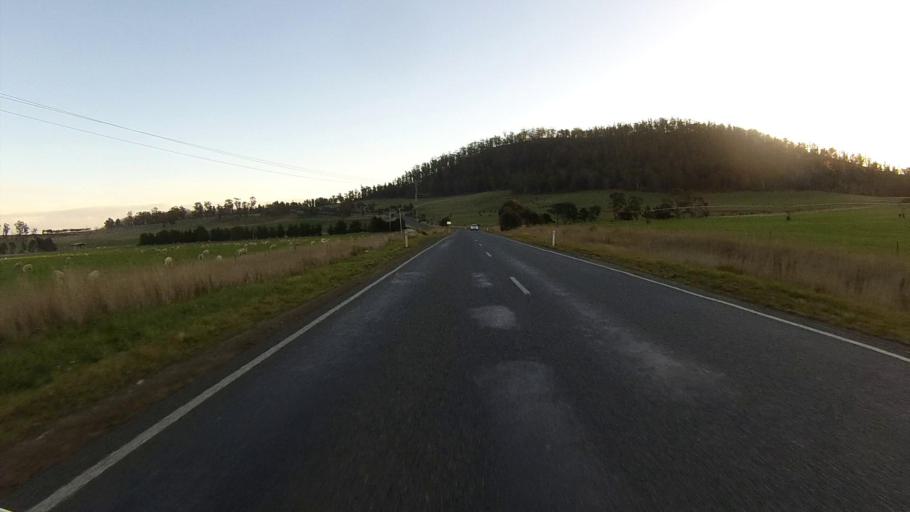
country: AU
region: Tasmania
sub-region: Sorell
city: Sorell
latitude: -42.8183
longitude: 147.7505
